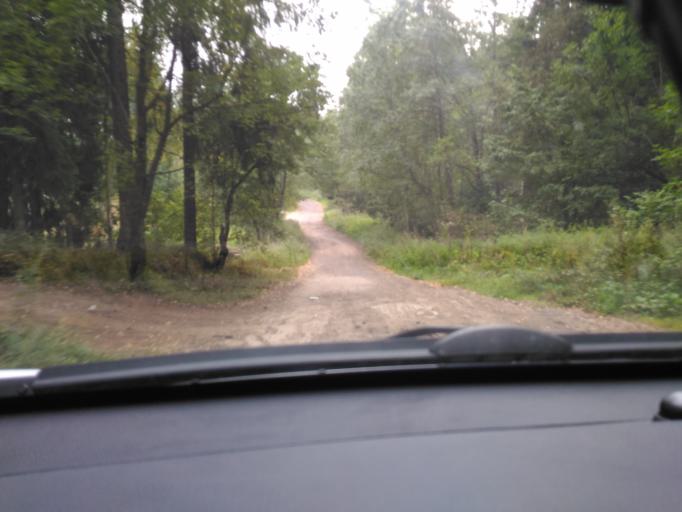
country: RU
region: Moskovskaya
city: Povarovo
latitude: 56.0933
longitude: 37.0572
